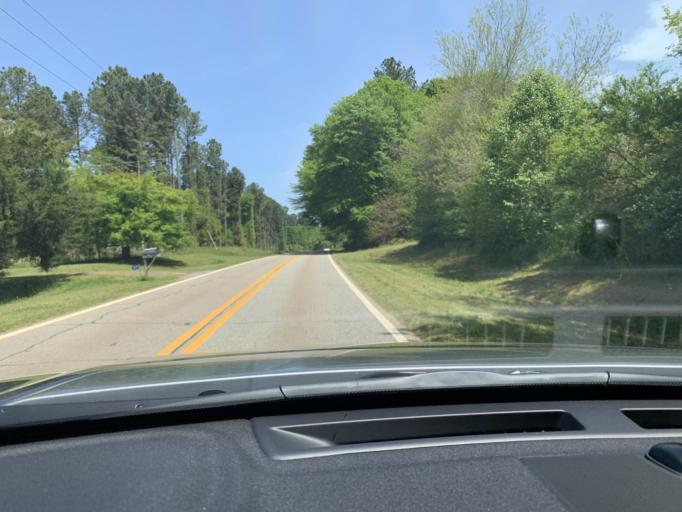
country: US
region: Georgia
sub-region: Oconee County
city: Bogart
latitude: 33.9168
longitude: -83.5626
